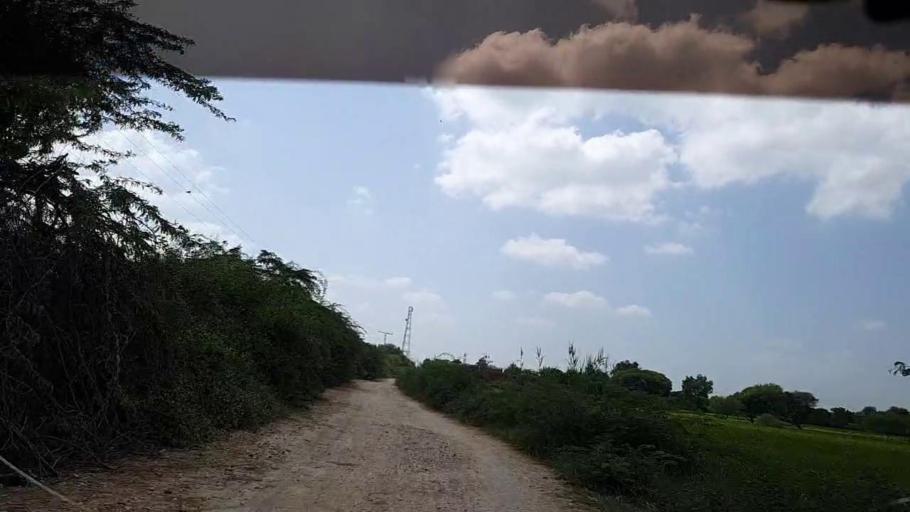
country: PK
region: Sindh
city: Badin
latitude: 24.5737
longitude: 68.7697
